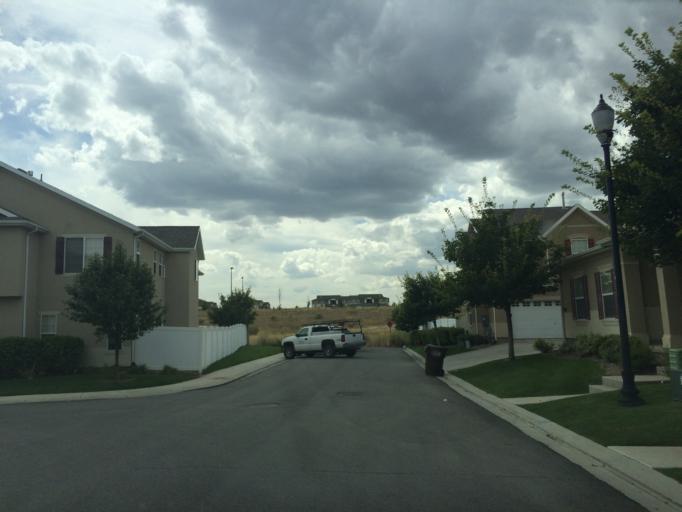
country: US
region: Utah
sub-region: Salt Lake County
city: Oquirrh
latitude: 40.6107
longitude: -112.0546
